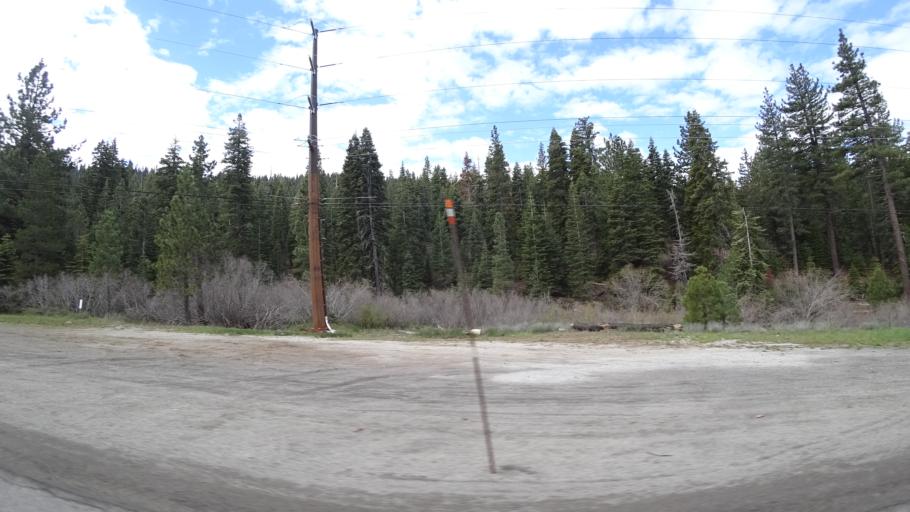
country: US
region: California
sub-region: Placer County
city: Tahoe Vista
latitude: 39.2732
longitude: -120.0999
